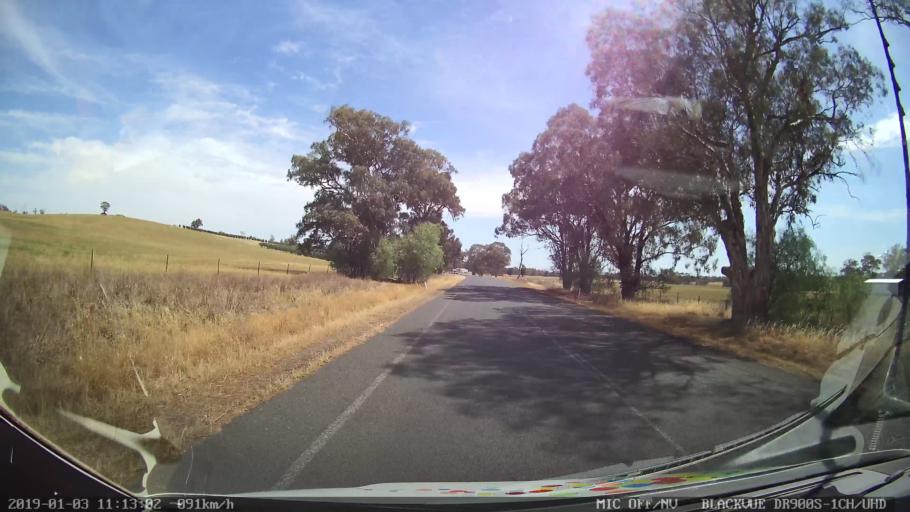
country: AU
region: New South Wales
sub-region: Young
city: Young
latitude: -34.1939
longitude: 148.2616
